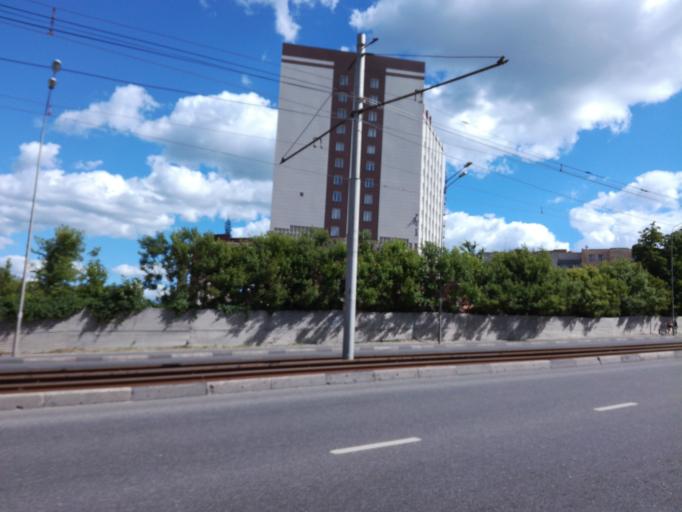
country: RU
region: Kursk
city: Kursk
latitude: 51.7539
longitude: 36.2025
